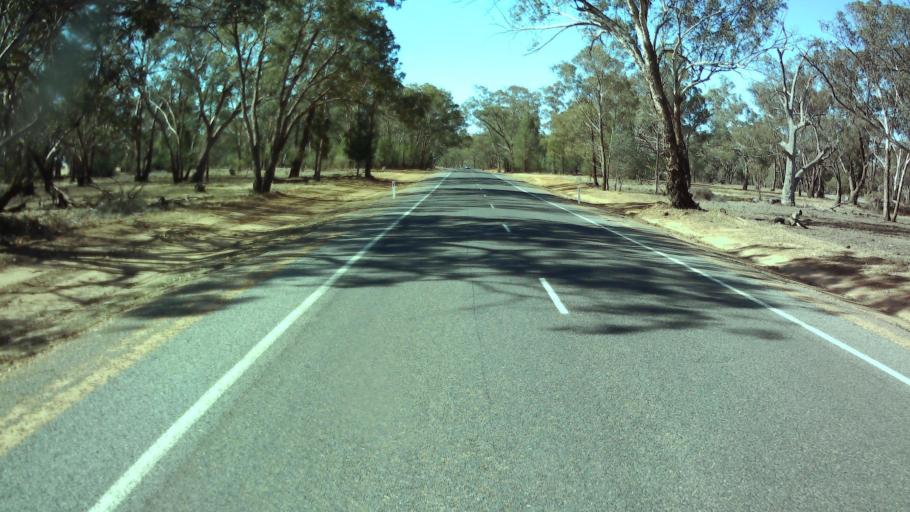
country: AU
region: New South Wales
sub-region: Weddin
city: Grenfell
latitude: -33.7615
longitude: 148.0821
